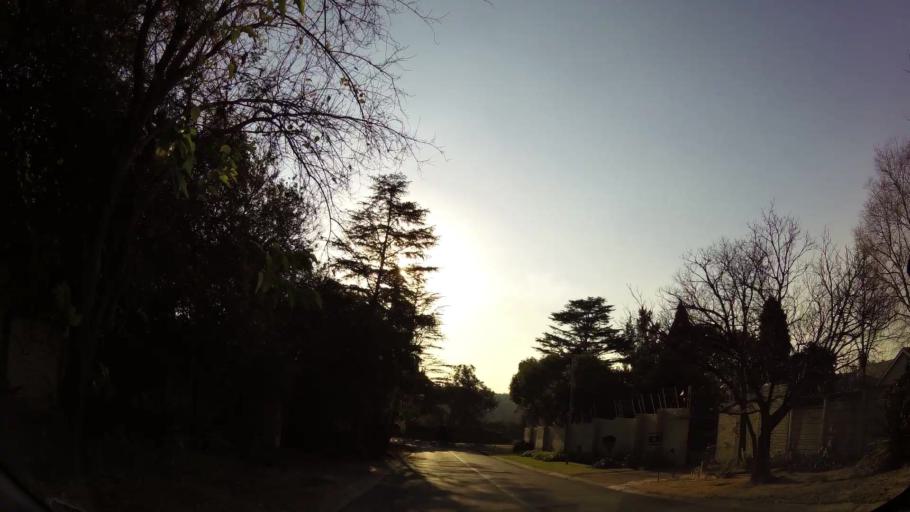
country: ZA
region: Gauteng
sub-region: City of Johannesburg Metropolitan Municipality
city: Diepsloot
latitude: -26.0607
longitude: 27.9861
